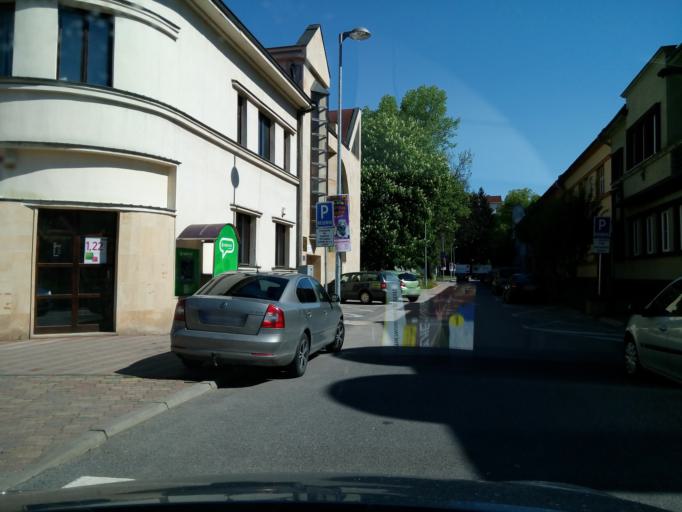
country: SK
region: Zilinsky
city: Ruzomberok
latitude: 49.0828
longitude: 19.2988
